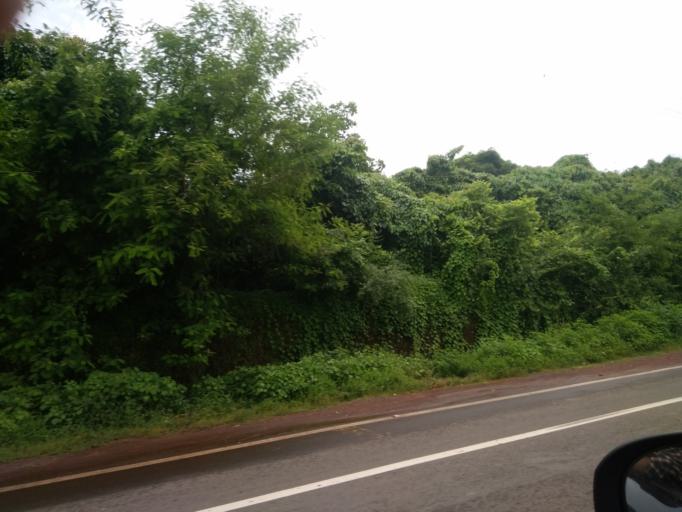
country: IN
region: Goa
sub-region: North Goa
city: Panaji
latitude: 15.5173
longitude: 73.8317
